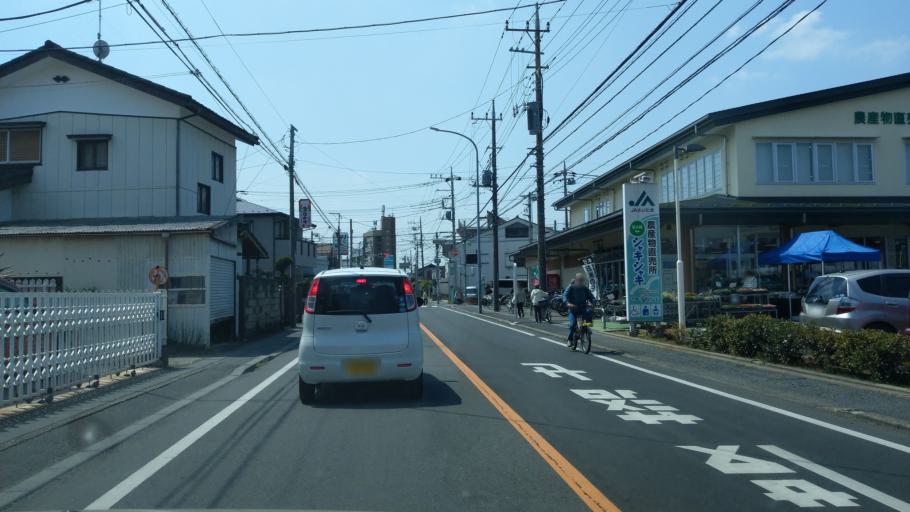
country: JP
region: Saitama
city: Yono
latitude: 35.8827
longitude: 139.6551
